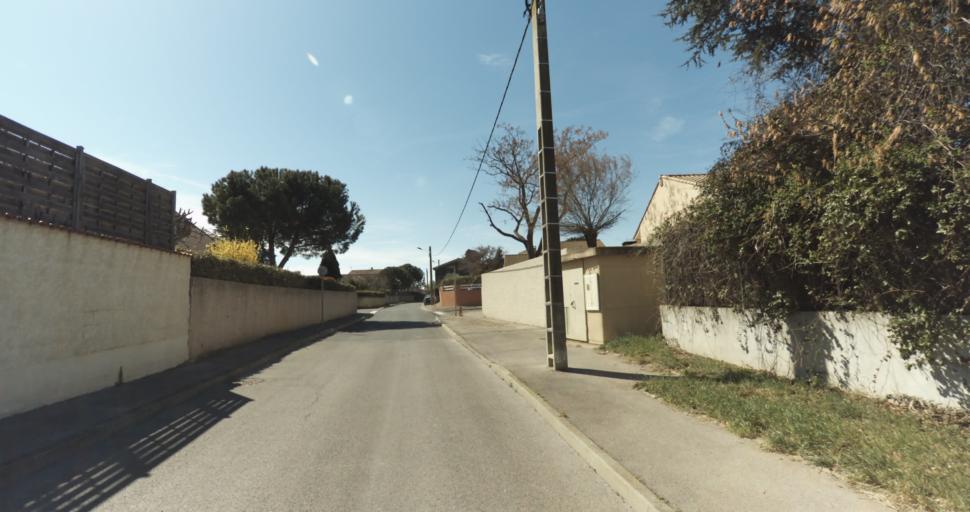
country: FR
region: Languedoc-Roussillon
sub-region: Departement de l'Herault
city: Marseillan
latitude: 43.3617
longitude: 3.5284
